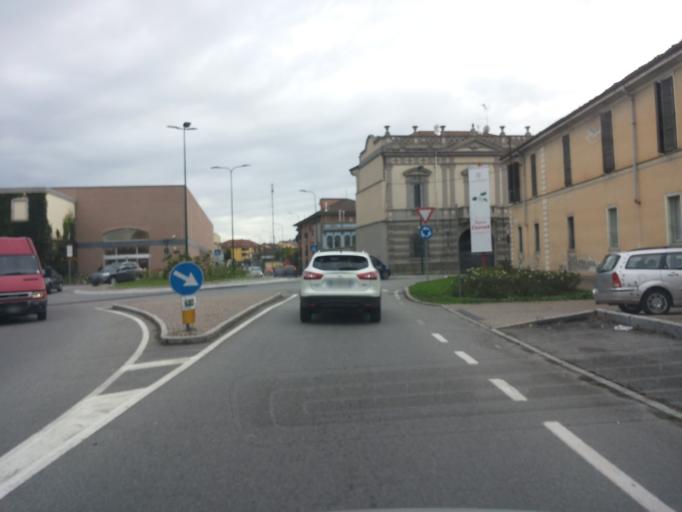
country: IT
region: Piedmont
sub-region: Provincia di Alessandria
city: Casale Monferrato
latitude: 45.1363
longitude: 8.4443
